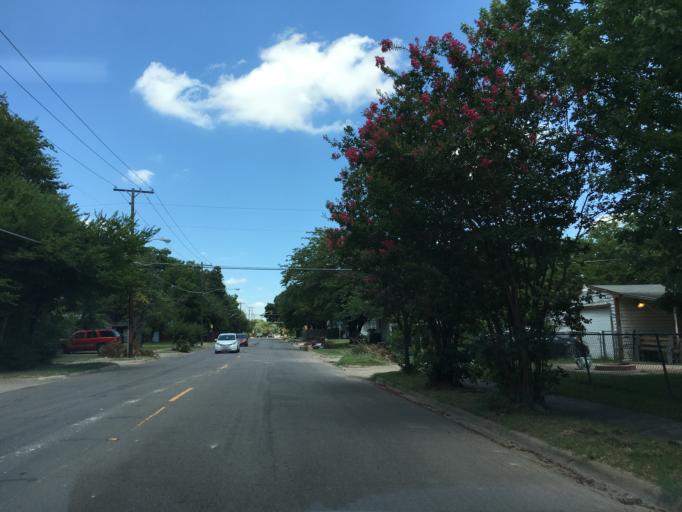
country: US
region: Texas
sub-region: Dallas County
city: Garland
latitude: 32.8403
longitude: -96.6731
